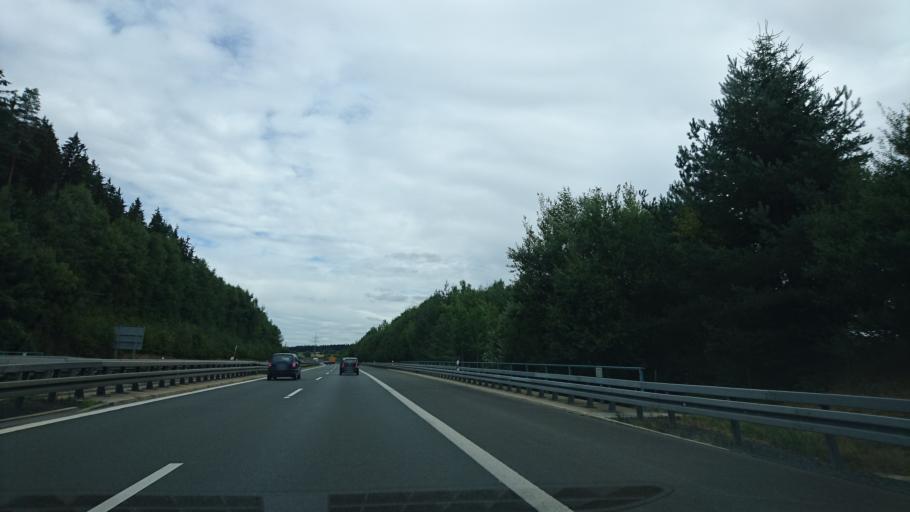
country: DE
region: Bavaria
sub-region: Upper Franconia
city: Thiersheim
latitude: 50.0478
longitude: 12.1038
